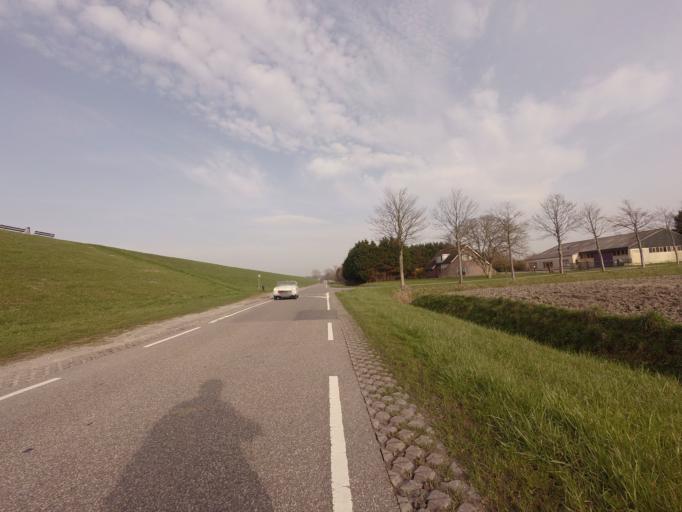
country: NL
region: Zeeland
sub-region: Gemeente Terneuzen
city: Zaamslag
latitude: 51.3647
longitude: 3.9505
